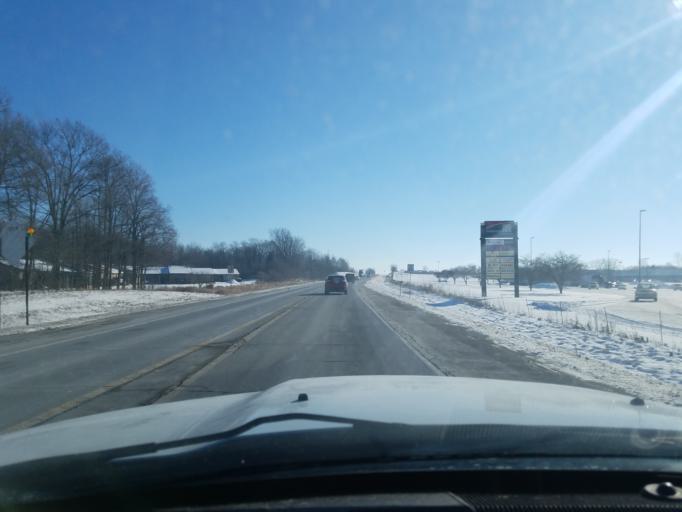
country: US
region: Indiana
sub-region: Noble County
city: Kendallville
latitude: 41.4511
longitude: -85.2455
